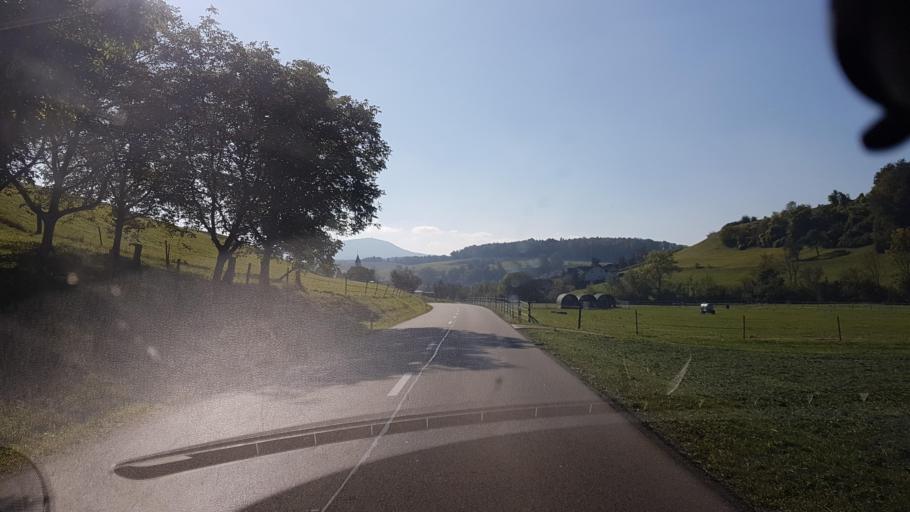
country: CH
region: Aargau
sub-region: Bezirk Laufenburg
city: Sulz
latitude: 47.4998
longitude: 8.0907
